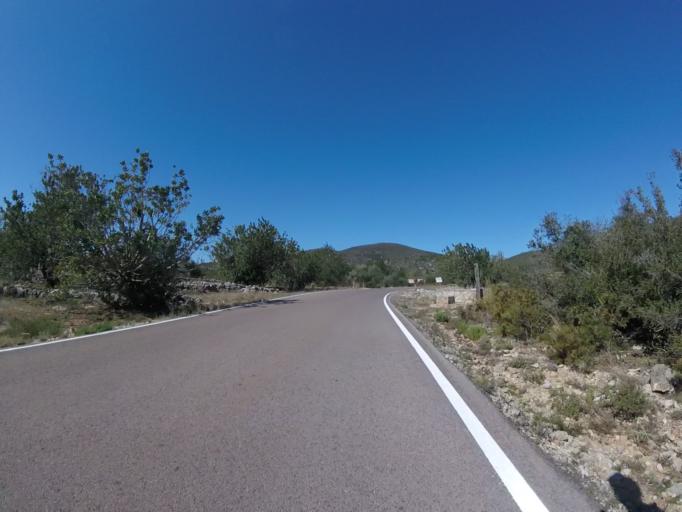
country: ES
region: Valencia
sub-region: Provincia de Castello
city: Santa Magdalena de Pulpis
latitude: 40.3802
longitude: 0.2664
